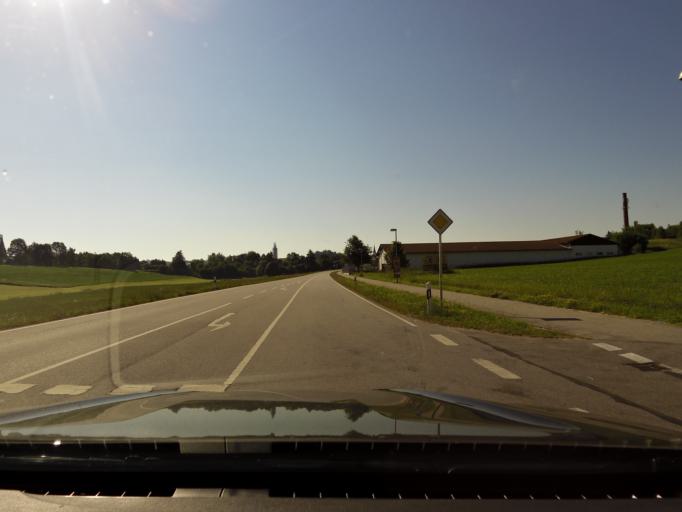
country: DE
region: Bavaria
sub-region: Upper Bavaria
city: Neumarkt-Sankt Veit
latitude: 48.3655
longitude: 12.5006
